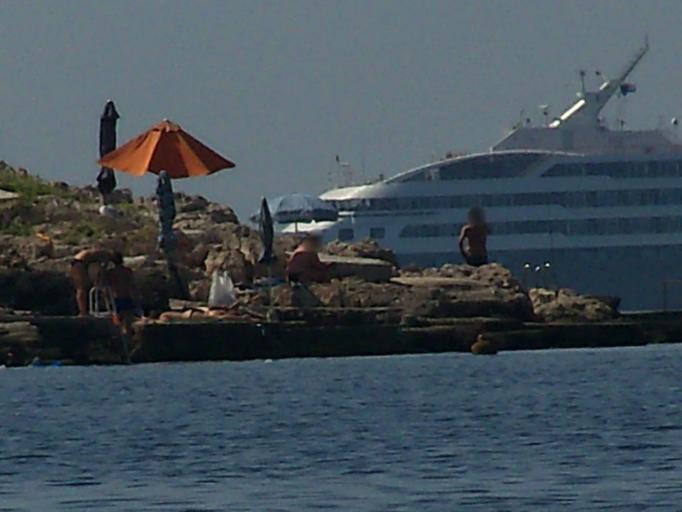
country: HR
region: Sibensko-Kniniska
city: Rogoznica
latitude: 43.4929
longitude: 16.0187
